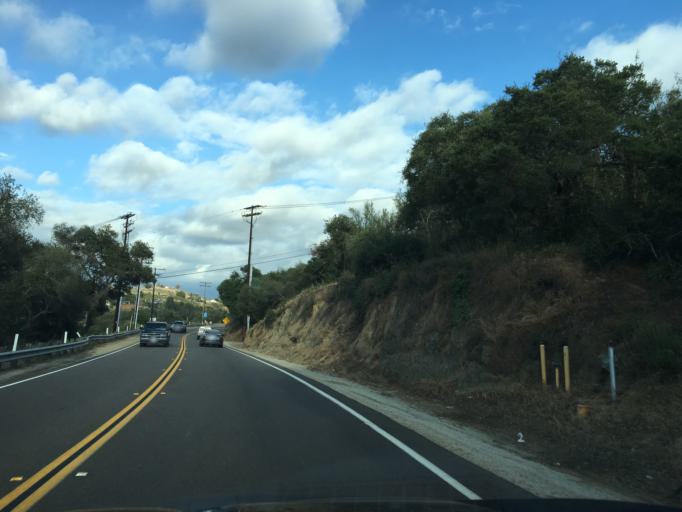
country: US
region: California
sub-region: San Diego County
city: Valley Center
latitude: 33.2497
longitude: -117.0593
